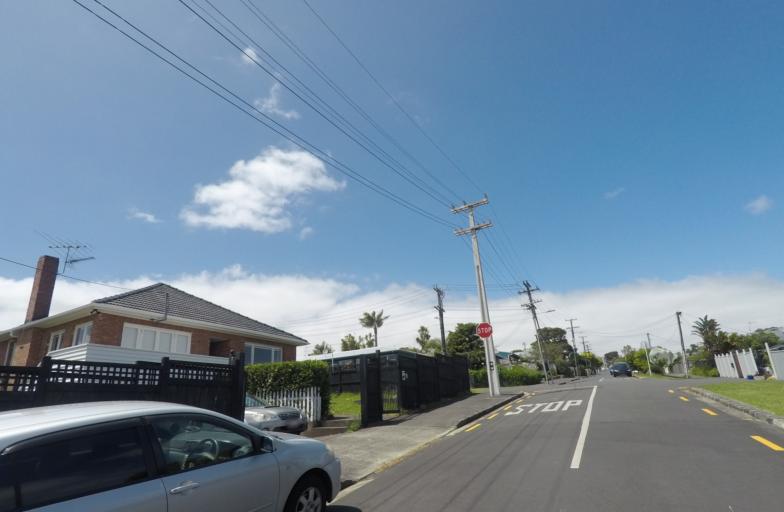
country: NZ
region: Auckland
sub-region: Auckland
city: Auckland
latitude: -36.8695
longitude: 174.7377
